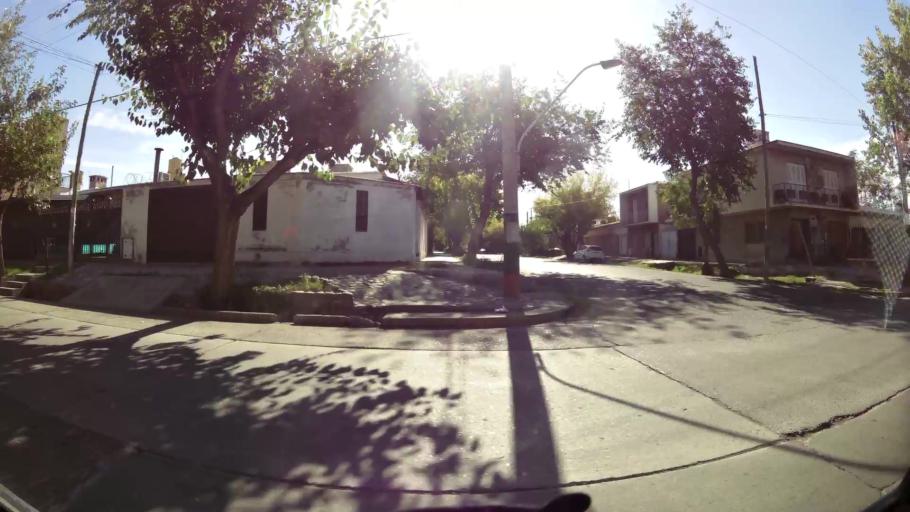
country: AR
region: Mendoza
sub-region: Departamento de Godoy Cruz
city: Godoy Cruz
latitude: -32.9117
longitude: -68.8331
